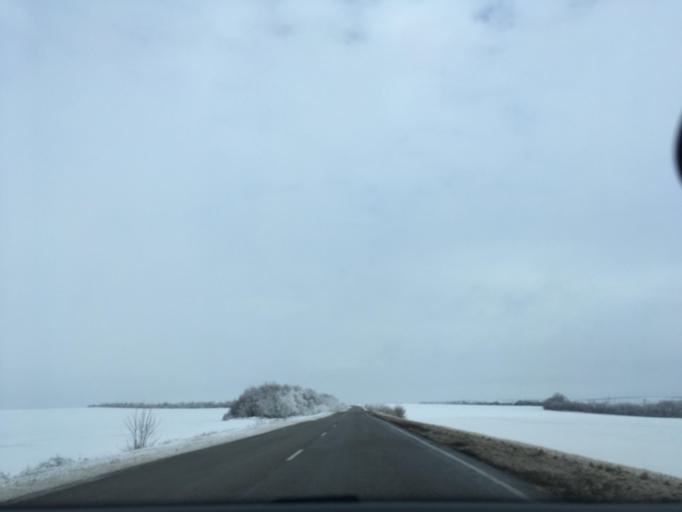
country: UA
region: Luhansk
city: Lozno-Oleksandrivka
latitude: 49.9946
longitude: 39.0319
